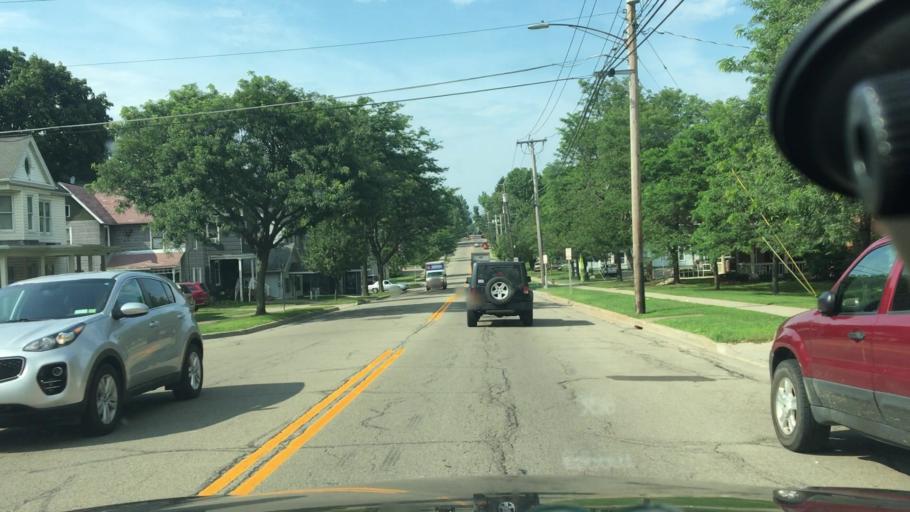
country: US
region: New York
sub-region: Chautauqua County
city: Jamestown
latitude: 42.1019
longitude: -79.2414
